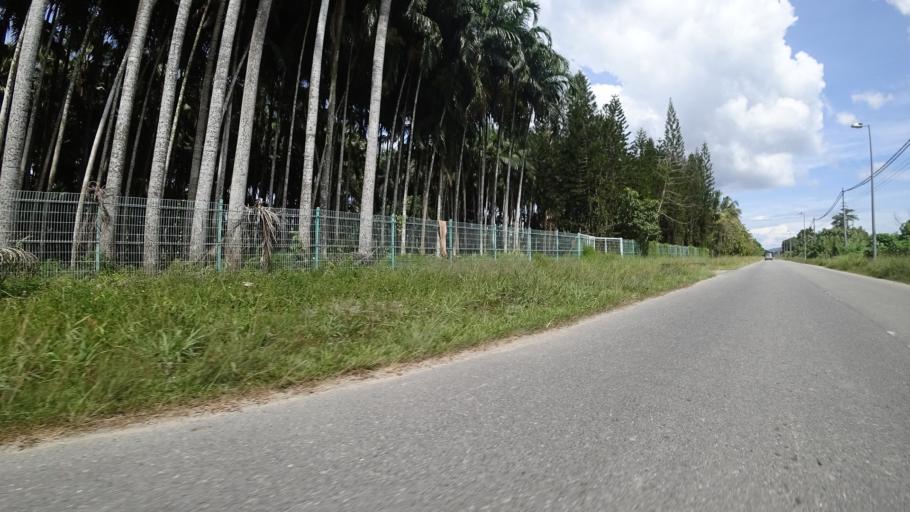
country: BN
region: Brunei and Muara
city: Bandar Seri Begawan
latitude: 4.8438
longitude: 114.8502
